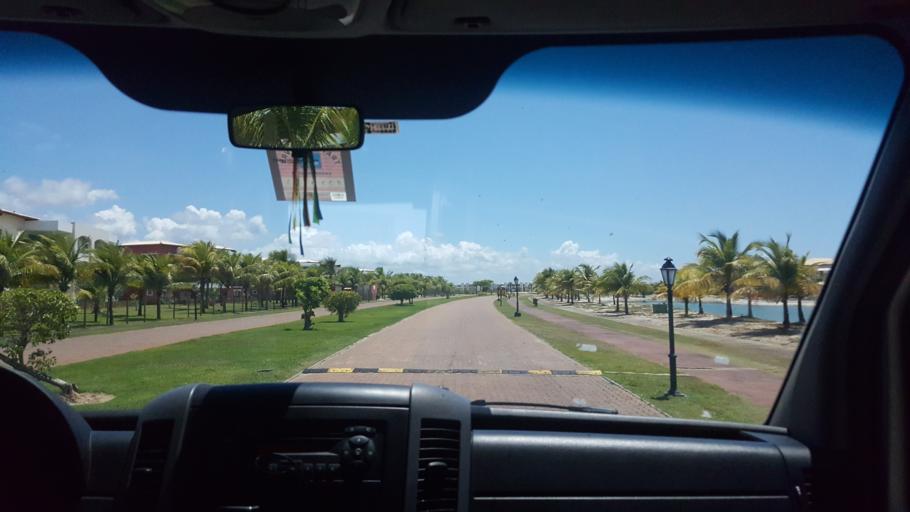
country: BR
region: Bahia
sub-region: Mata De Sao Joao
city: Mata de Sao Joao
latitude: -12.5466
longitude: -37.9890
